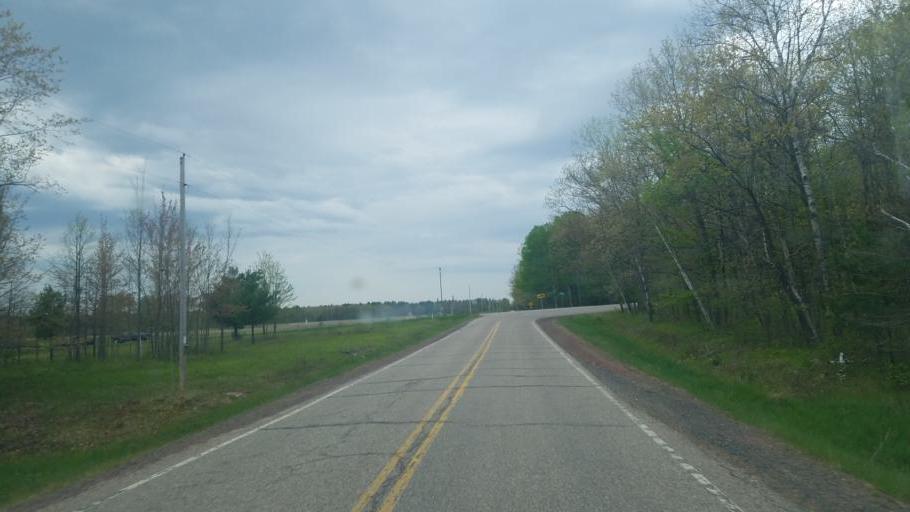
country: US
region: Wisconsin
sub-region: Wood County
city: Marshfield
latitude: 44.5126
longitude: -90.2979
